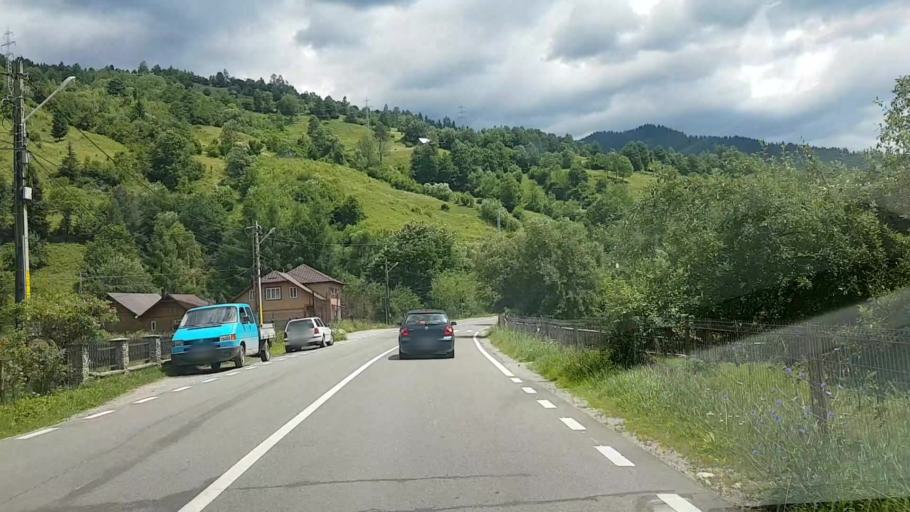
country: RO
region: Suceava
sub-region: Comuna Brosteni
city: Brosteni
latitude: 47.2609
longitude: 25.6861
